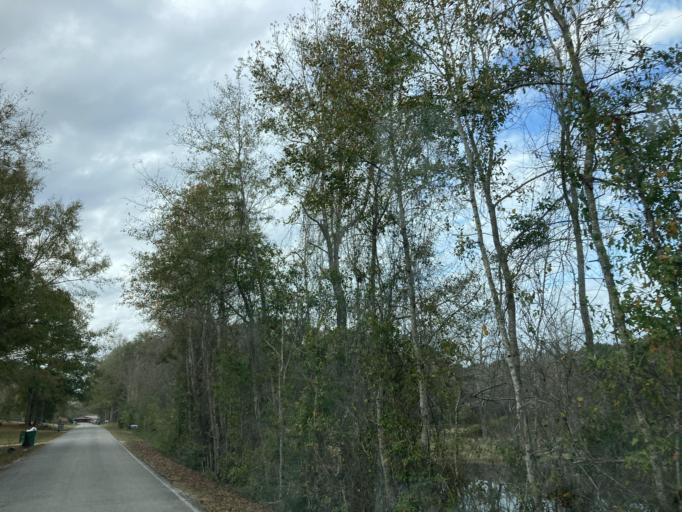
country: US
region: Mississippi
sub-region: Stone County
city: Wiggins
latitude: 30.9944
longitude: -89.2550
